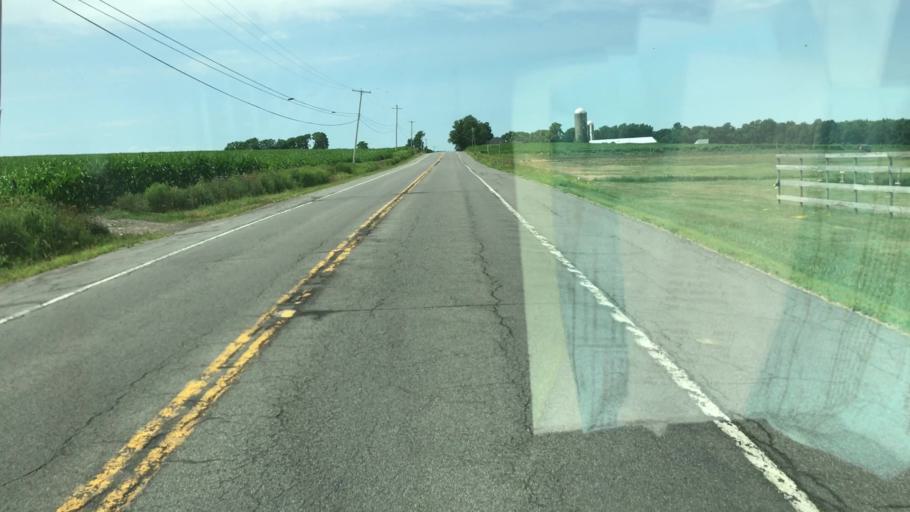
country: US
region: New York
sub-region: Onondaga County
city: Marcellus
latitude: 42.9229
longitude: -76.2616
